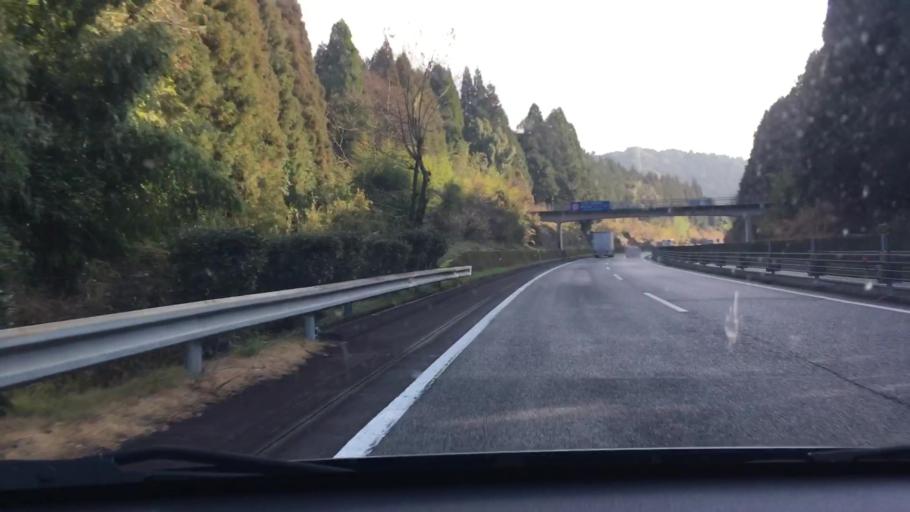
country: JP
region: Kagoshima
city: Okuchi-shinohara
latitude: 31.9989
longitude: 130.7587
